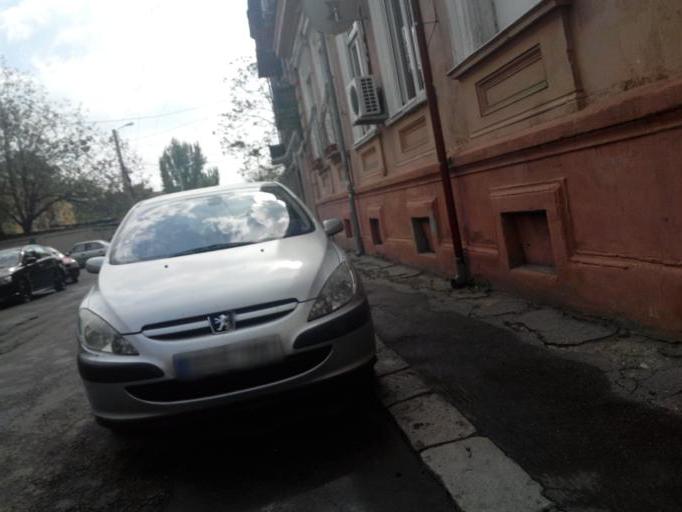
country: RO
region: Bucuresti
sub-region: Municipiul Bucuresti
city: Bucuresti
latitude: 44.4255
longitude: 26.0954
